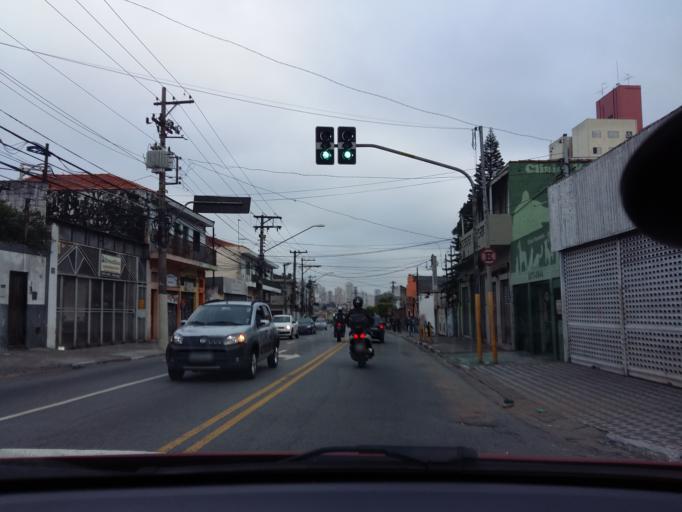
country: BR
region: Sao Paulo
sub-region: Diadema
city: Diadema
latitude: -23.6313
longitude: -46.6275
